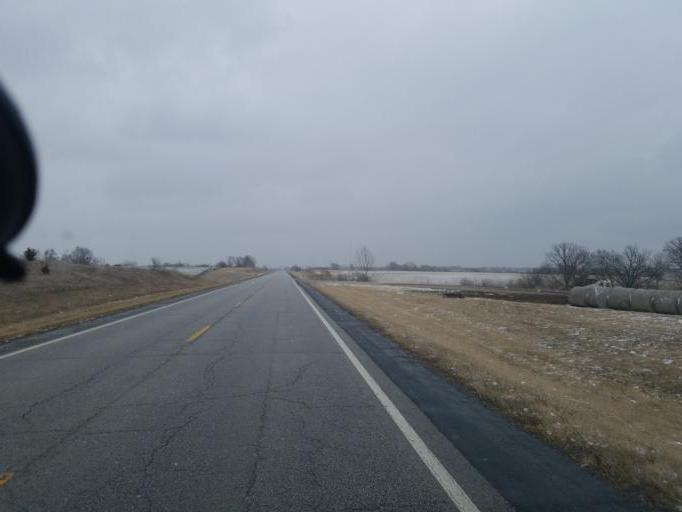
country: US
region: Missouri
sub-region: Putnam County
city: Unionville
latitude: 40.4666
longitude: -92.8312
